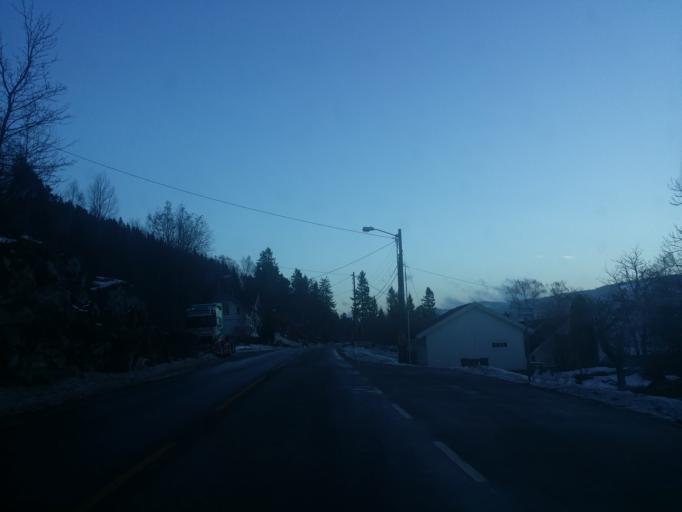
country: NO
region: Buskerud
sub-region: Hole
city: Vik
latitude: 60.0120
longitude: 10.2655
